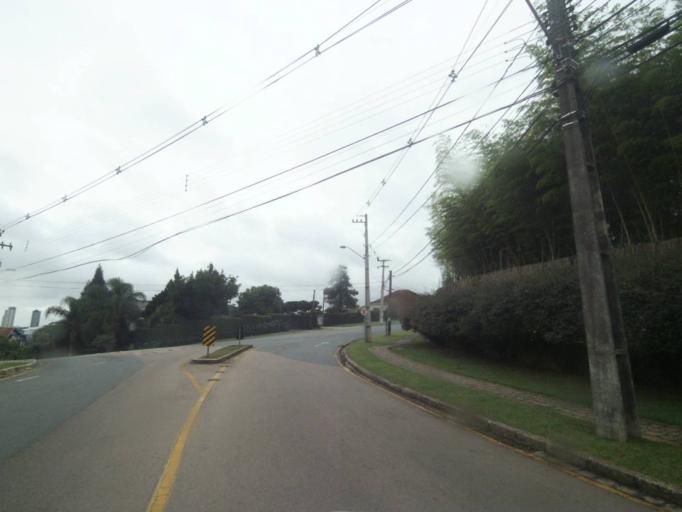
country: BR
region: Parana
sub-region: Curitiba
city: Curitiba
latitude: -25.4217
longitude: -49.3257
